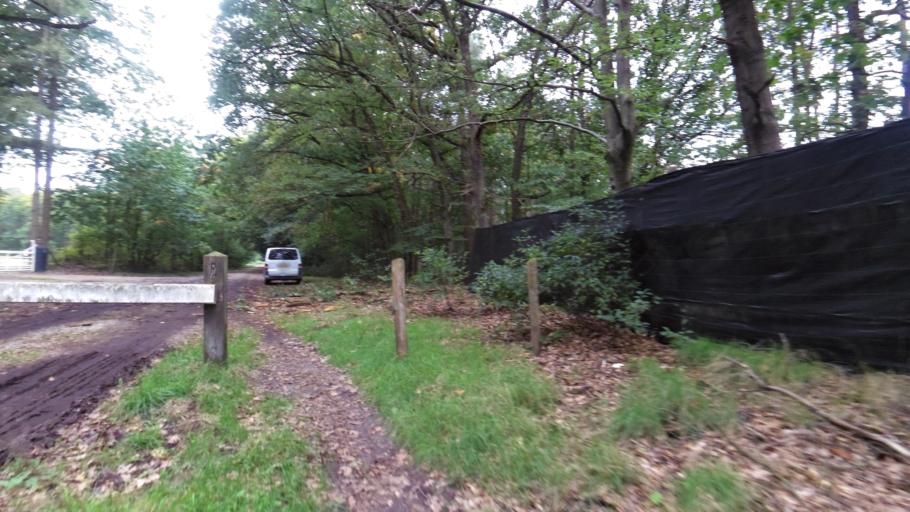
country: NL
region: Gelderland
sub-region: Gemeente Apeldoorn
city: Beekbergen
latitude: 52.1847
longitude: 5.8885
